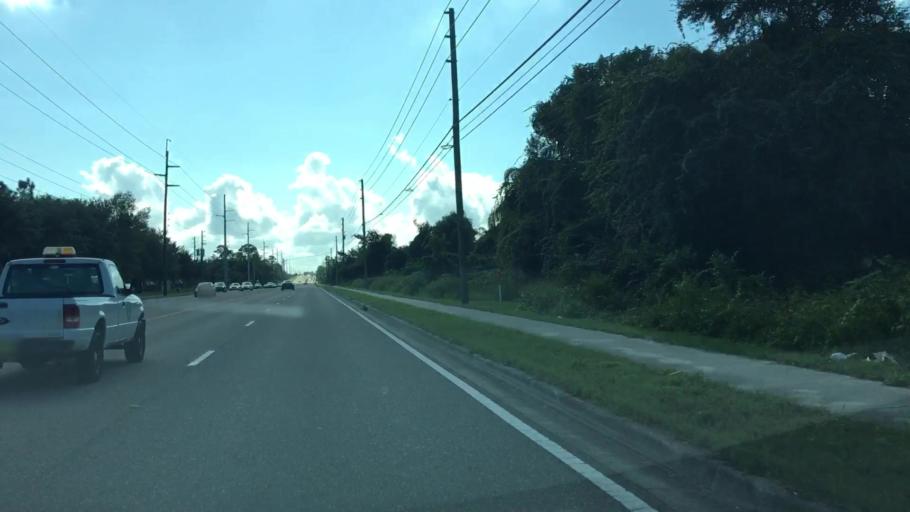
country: US
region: Florida
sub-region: Volusia County
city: Deltona
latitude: 28.8963
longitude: -81.2842
